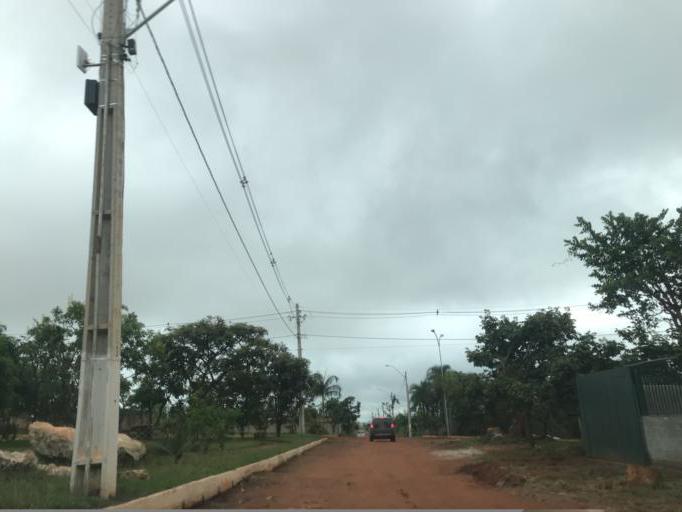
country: BR
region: Federal District
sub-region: Brasilia
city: Brasilia
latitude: -15.8274
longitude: -47.7902
